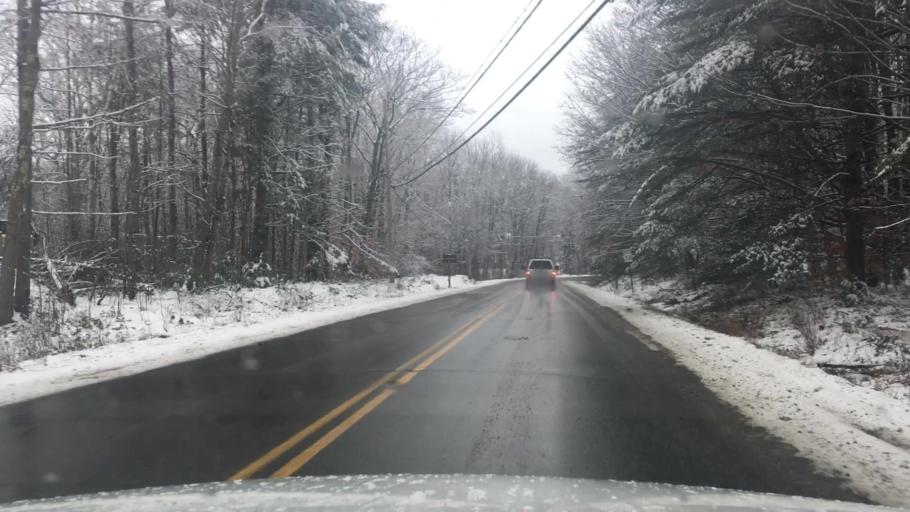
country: US
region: Maine
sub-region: Lincoln County
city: Jefferson
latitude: 44.1935
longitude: -69.4502
